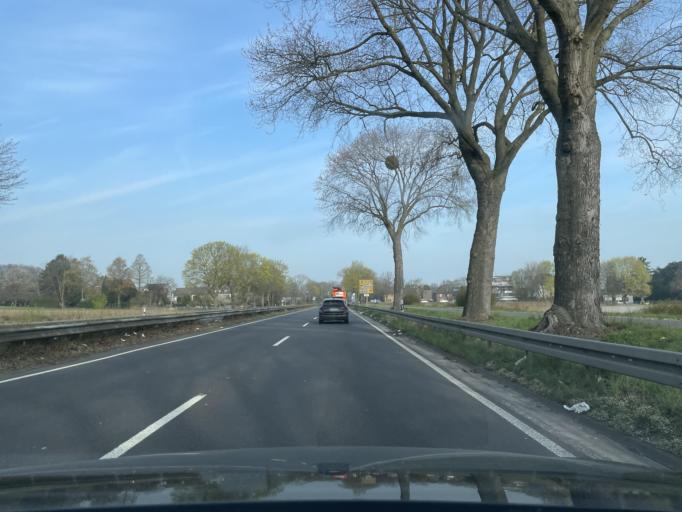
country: DE
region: North Rhine-Westphalia
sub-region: Regierungsbezirk Dusseldorf
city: Viersen
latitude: 51.2281
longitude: 6.4260
